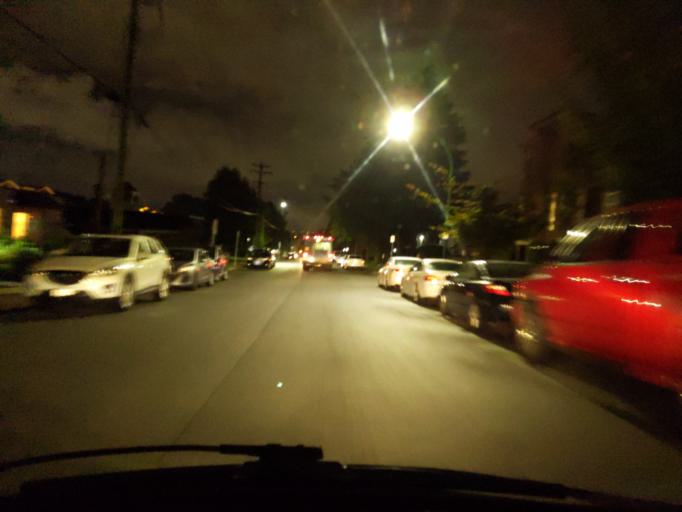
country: CA
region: British Columbia
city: Burnaby
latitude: 49.2542
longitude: -123.0224
